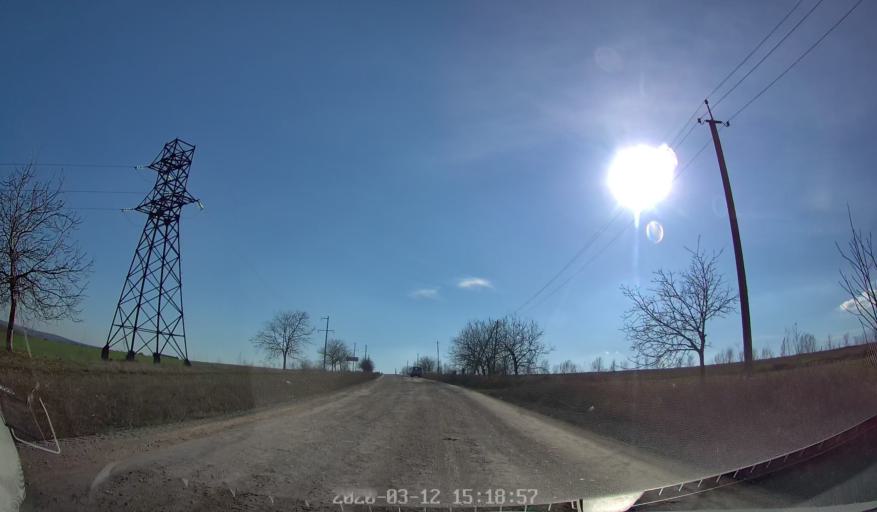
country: MD
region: Chisinau
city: Ciorescu
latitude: 47.2155
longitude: 28.9312
